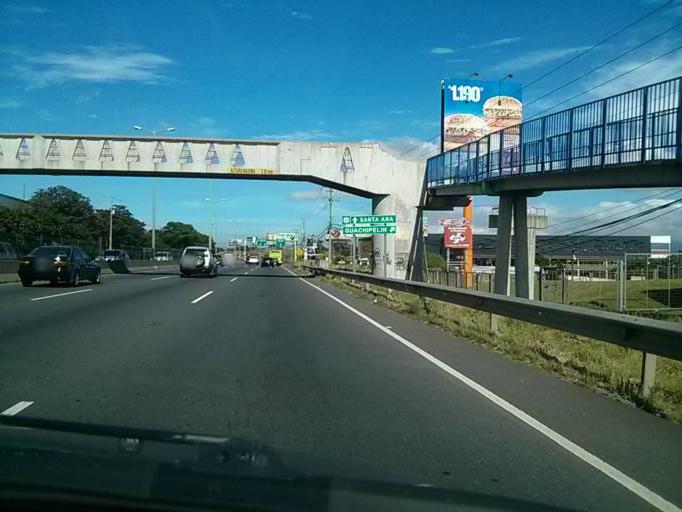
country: CR
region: San Jose
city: San Rafael
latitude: 9.9449
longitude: -84.1495
